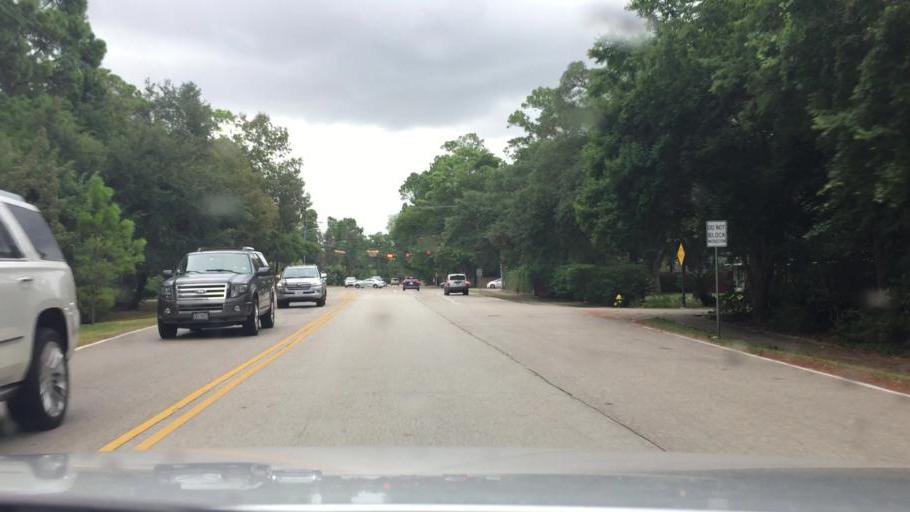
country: US
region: Texas
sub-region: Harris County
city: Hunters Creek Village
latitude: 29.7650
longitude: -95.5023
